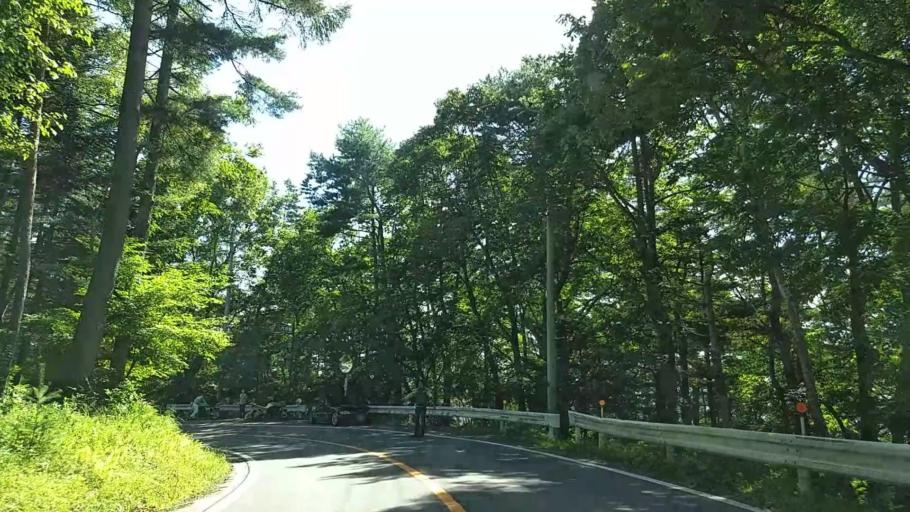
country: JP
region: Nagano
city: Chino
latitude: 36.0542
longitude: 138.2682
